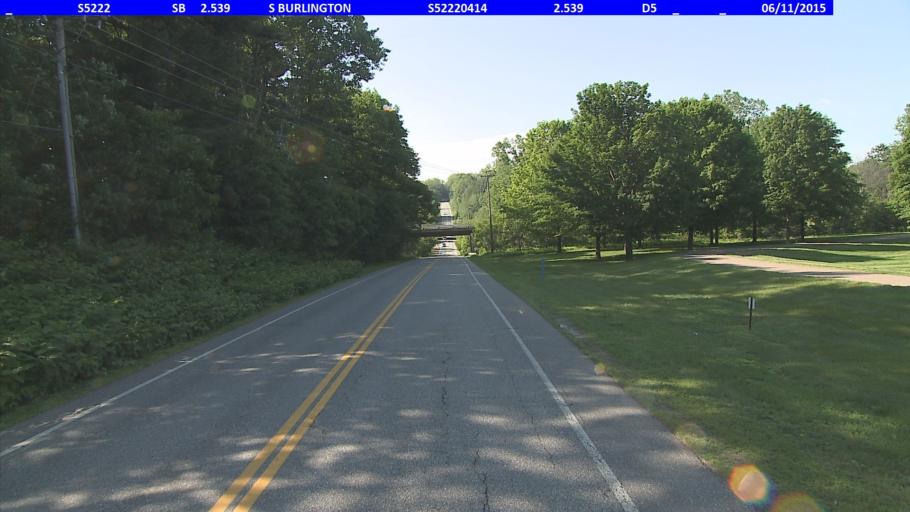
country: US
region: Vermont
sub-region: Chittenden County
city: South Burlington
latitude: 44.4529
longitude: -73.1889
